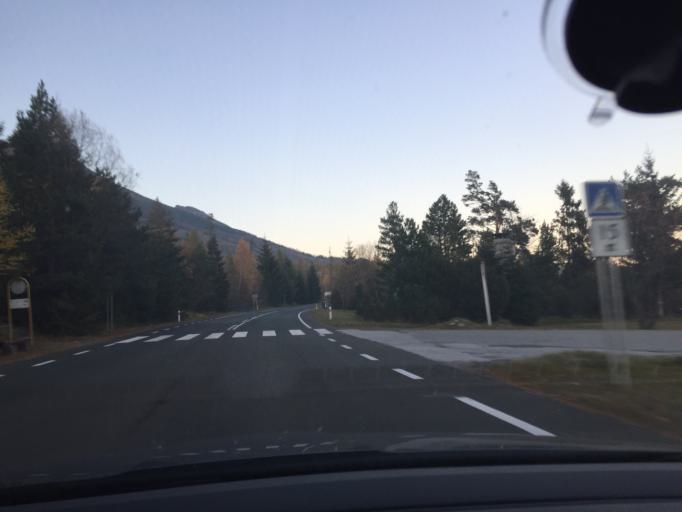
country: SK
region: Presovsky
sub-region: Okres Poprad
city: Vysoke Tatry
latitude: 49.1299
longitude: 20.1985
